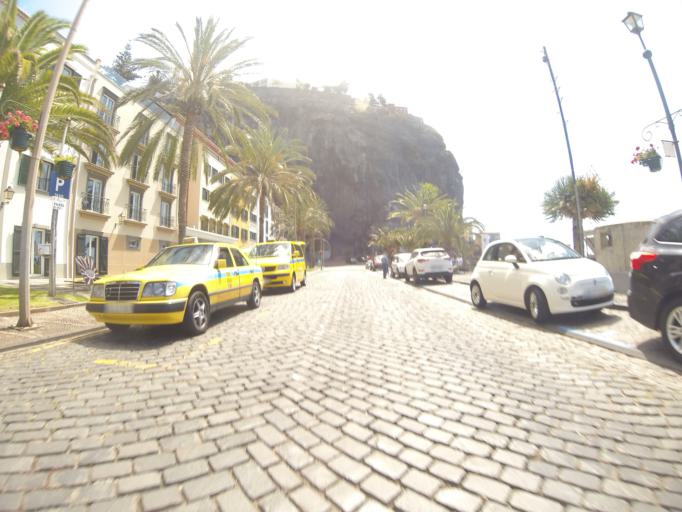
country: PT
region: Madeira
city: Ponta do Sol
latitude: 32.6799
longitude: -17.1043
